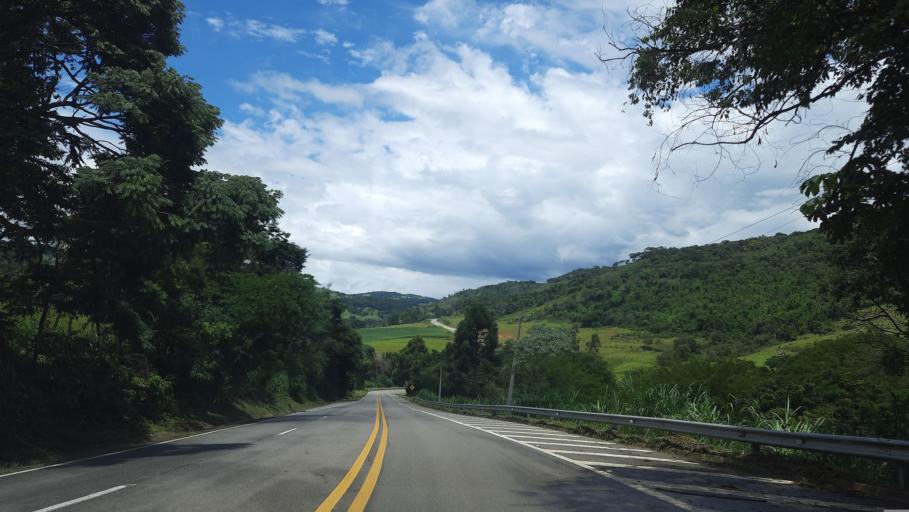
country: BR
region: Sao Paulo
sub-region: Vargem Grande Do Sul
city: Vargem Grande do Sul
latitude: -21.8262
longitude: -46.7776
